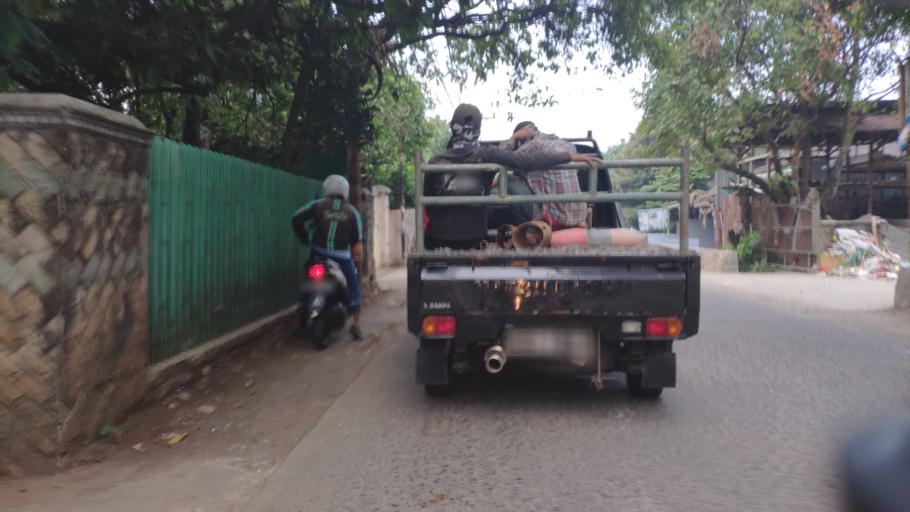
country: ID
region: West Java
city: Pamulang
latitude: -6.3192
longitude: 106.7952
